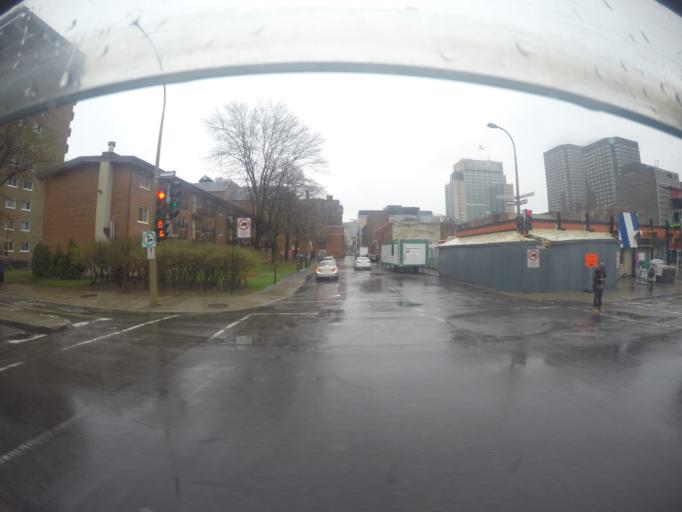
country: CA
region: Quebec
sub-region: Montreal
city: Montreal
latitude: 45.4919
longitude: -73.5794
